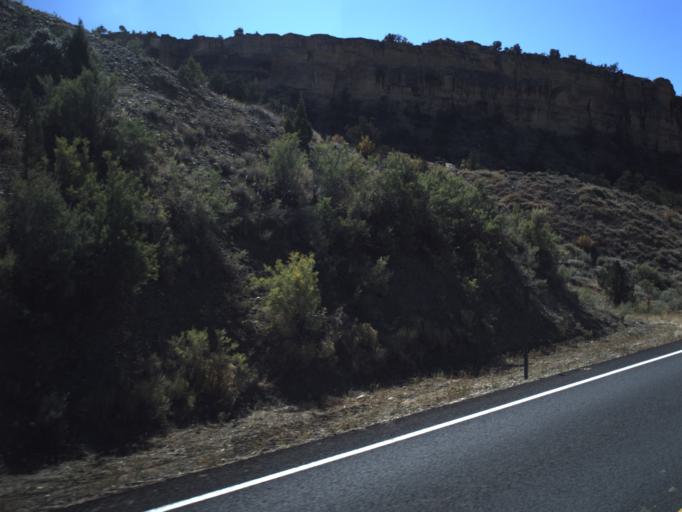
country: US
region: Utah
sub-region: Wayne County
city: Loa
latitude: 37.7664
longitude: -111.6740
